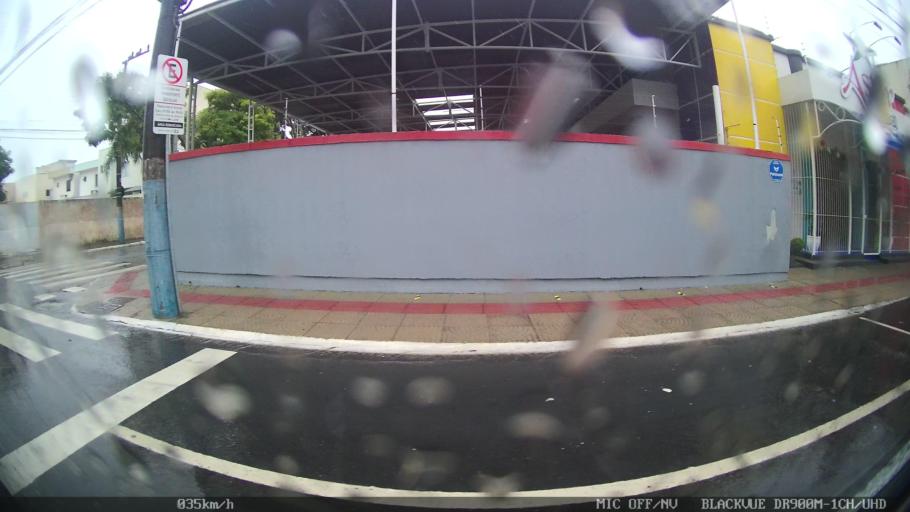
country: BR
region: Santa Catarina
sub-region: Balneario Camboriu
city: Balneario Camboriu
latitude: -26.9984
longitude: -48.6436
